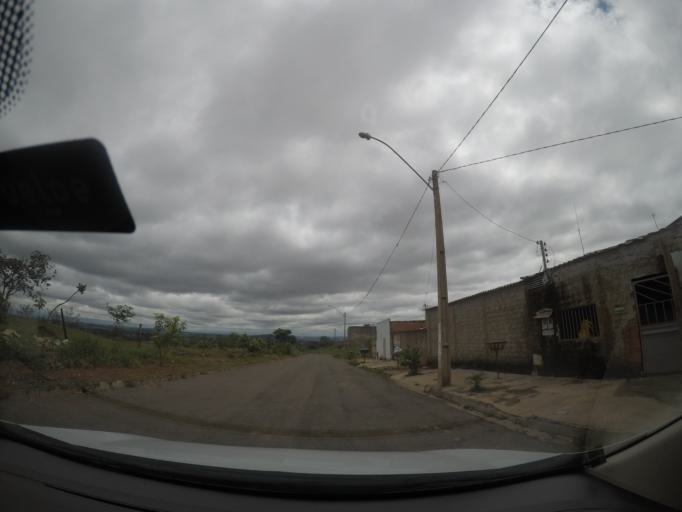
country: BR
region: Goias
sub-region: Trindade
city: Trindade
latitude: -16.7426
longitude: -49.3836
